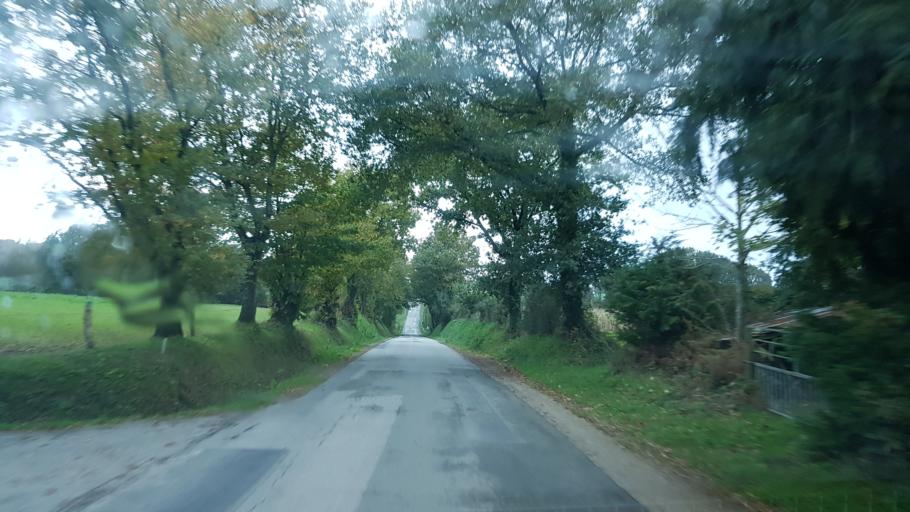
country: FR
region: Brittany
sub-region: Departement du Morbihan
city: Elven
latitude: 47.7329
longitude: -2.5755
